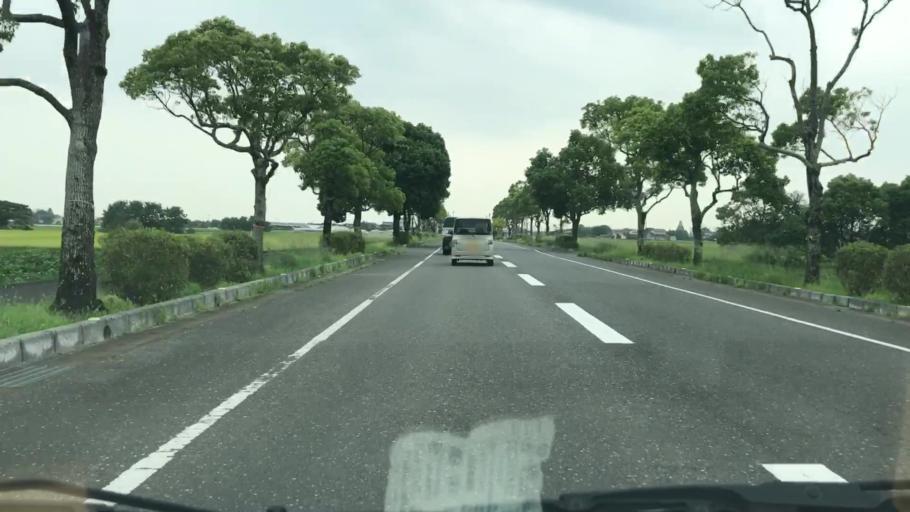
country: JP
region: Saga Prefecture
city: Saga-shi
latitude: 33.2308
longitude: 130.3060
